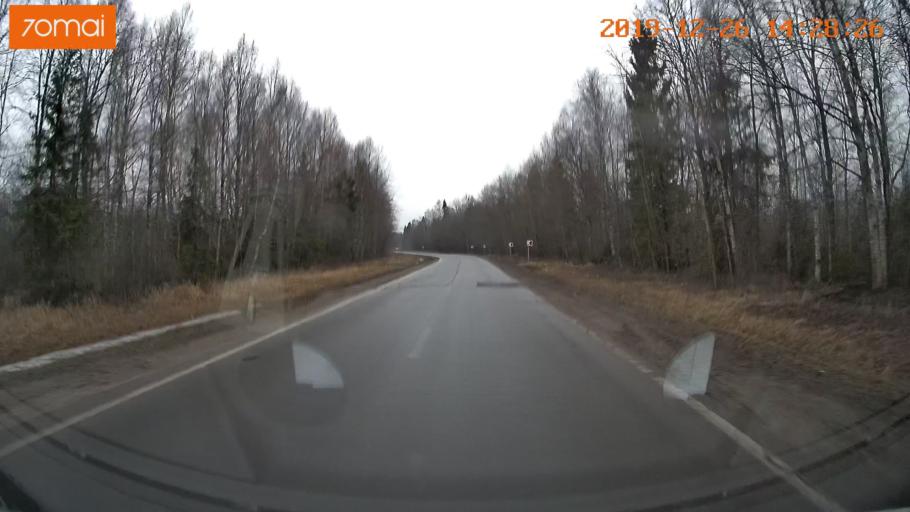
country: RU
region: Jaroslavl
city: Poshekhon'ye
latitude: 58.4754
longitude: 39.0533
